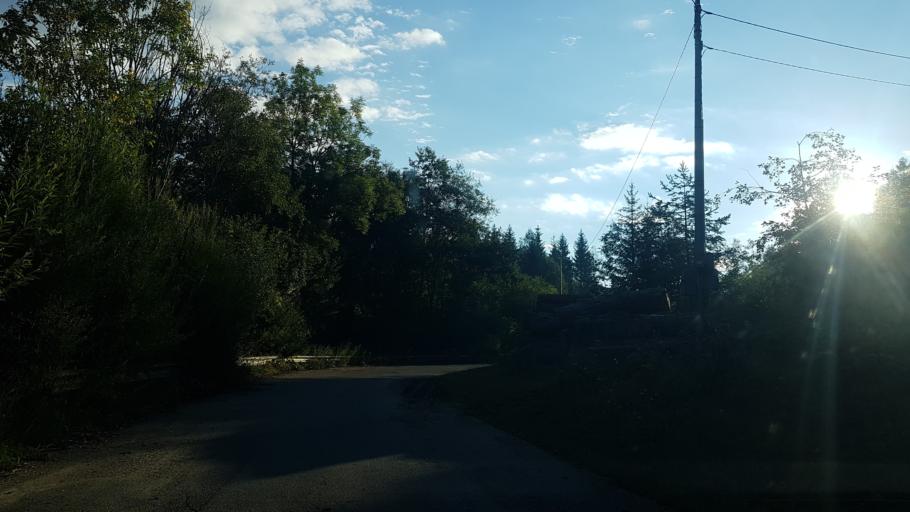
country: IT
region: Friuli Venezia Giulia
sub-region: Provincia di Udine
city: Tarvisio
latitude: 46.4920
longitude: 13.5921
